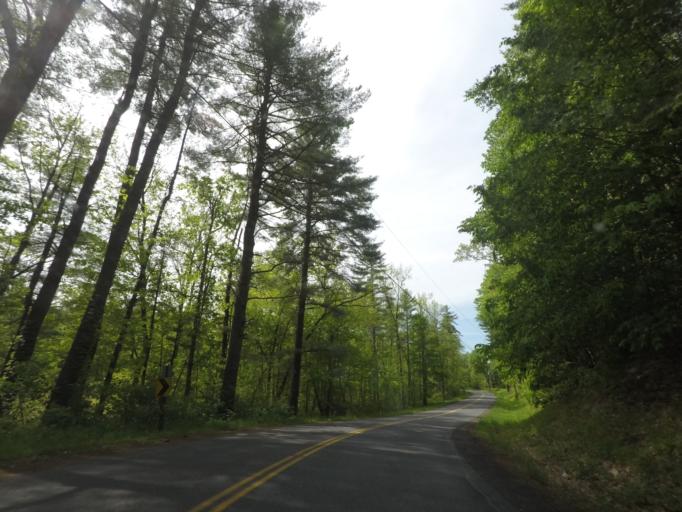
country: US
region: New York
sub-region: Saratoga County
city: Stillwater
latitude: 42.9853
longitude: -73.7145
